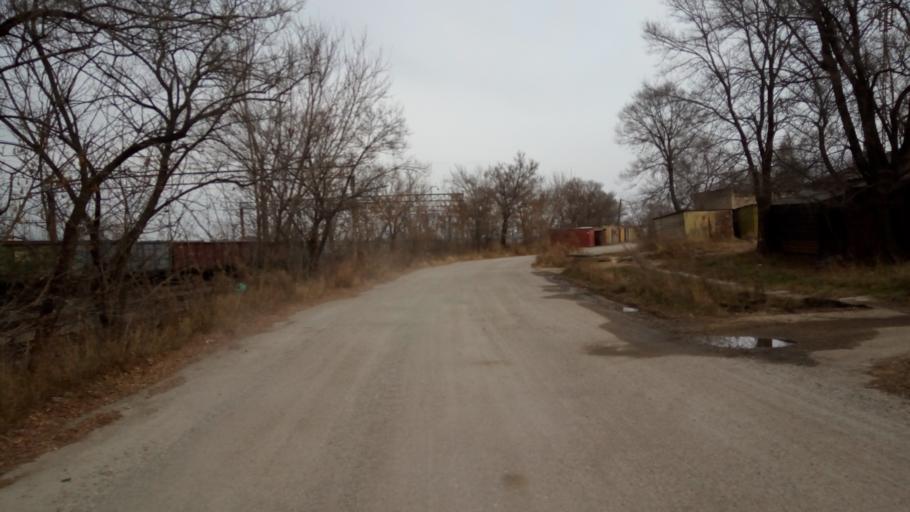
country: RU
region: Primorskiy
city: Novoshakhtinskiy
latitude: 44.0305
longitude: 132.1704
